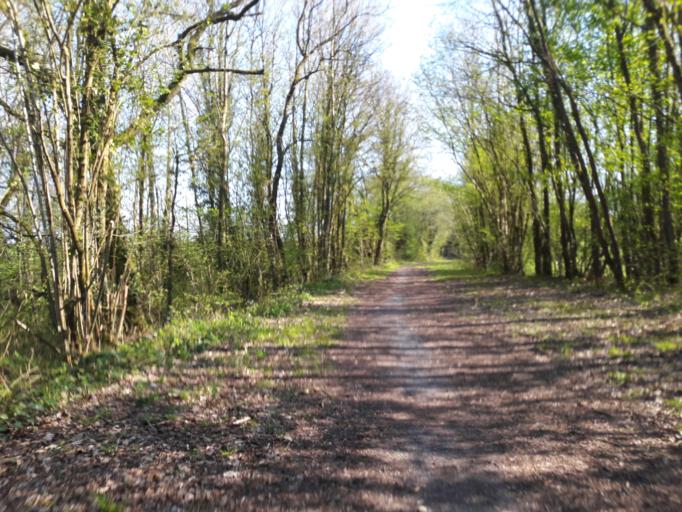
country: FR
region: Nord-Pas-de-Calais
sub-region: Departement du Nord
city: Sains-du-Nord
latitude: 50.1245
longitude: 4.0674
